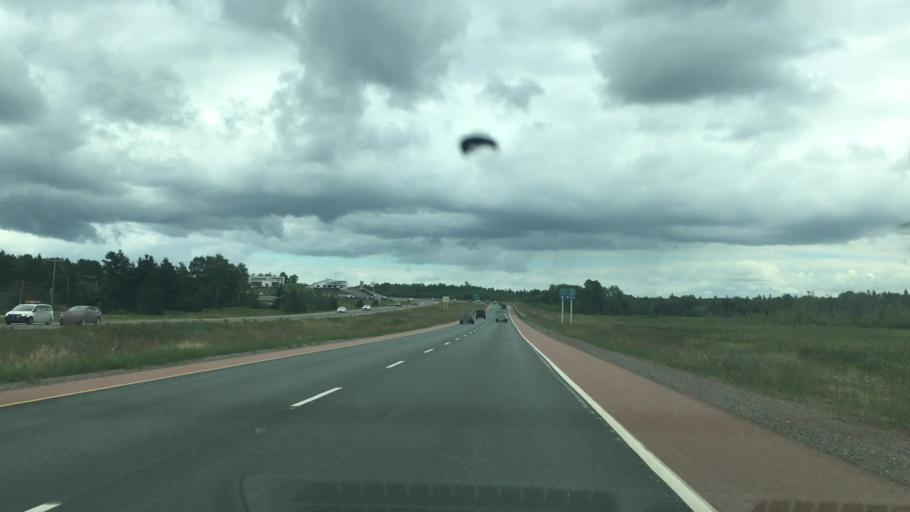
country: CA
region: Nova Scotia
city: Antigonish
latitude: 45.5970
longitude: -62.0390
